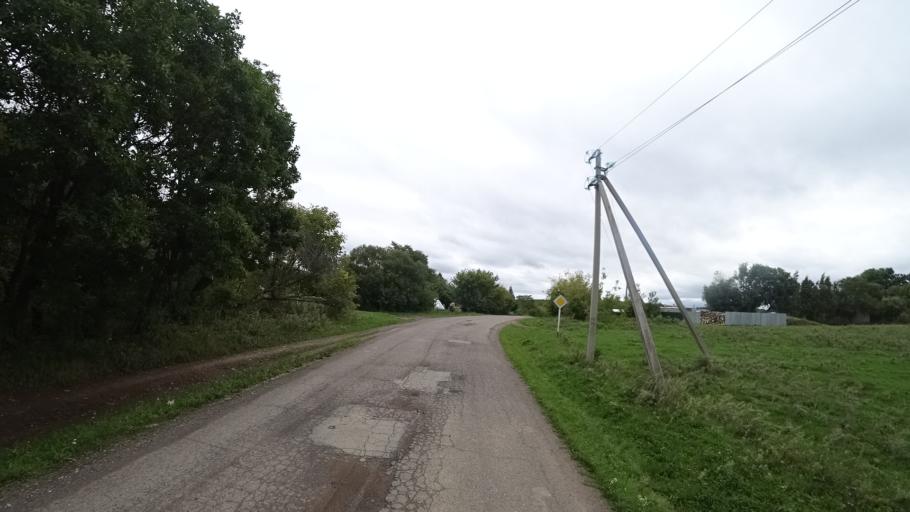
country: RU
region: Primorskiy
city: Chernigovka
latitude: 44.4639
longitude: 132.5902
